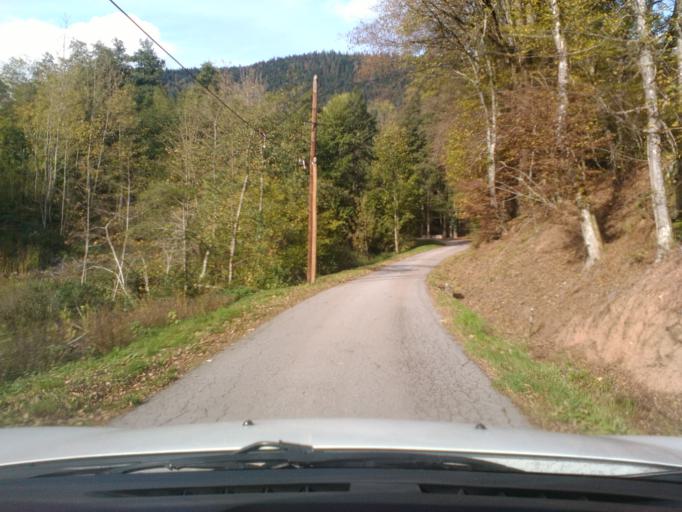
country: FR
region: Lorraine
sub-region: Departement des Vosges
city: Sainte-Marguerite
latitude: 48.2963
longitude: 7.0136
